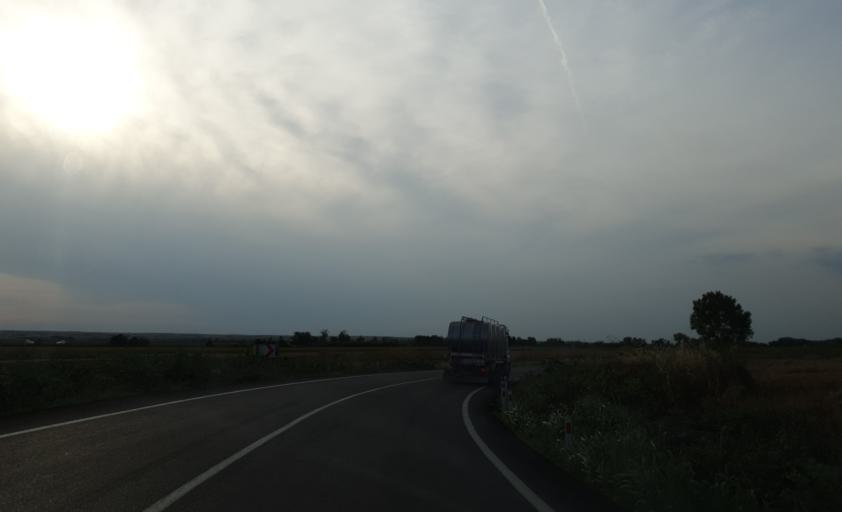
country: TR
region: Tekirdag
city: Hayrabolu
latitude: 41.2594
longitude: 27.1348
